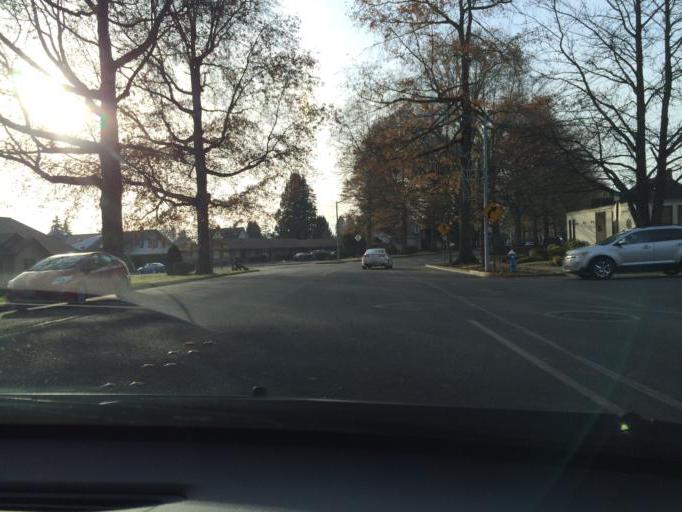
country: US
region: Washington
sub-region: Whatcom County
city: Lynden
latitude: 48.9399
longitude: -122.4626
